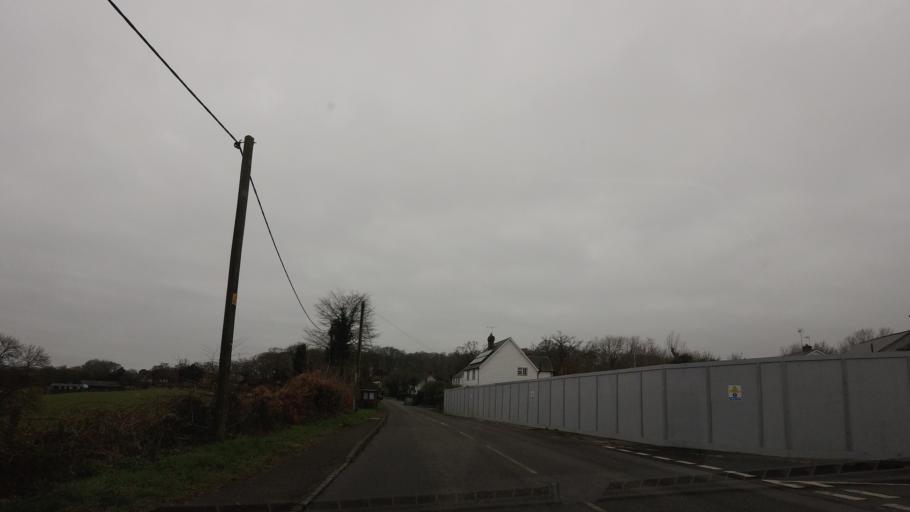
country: GB
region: England
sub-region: East Sussex
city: Robertsbridge
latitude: 50.9624
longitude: 0.5299
